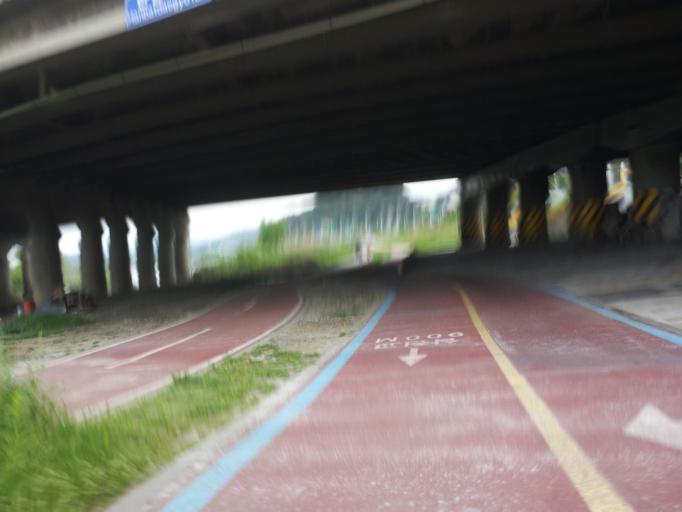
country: KR
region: Daejeon
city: Daejeon
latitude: 36.3566
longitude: 127.4046
